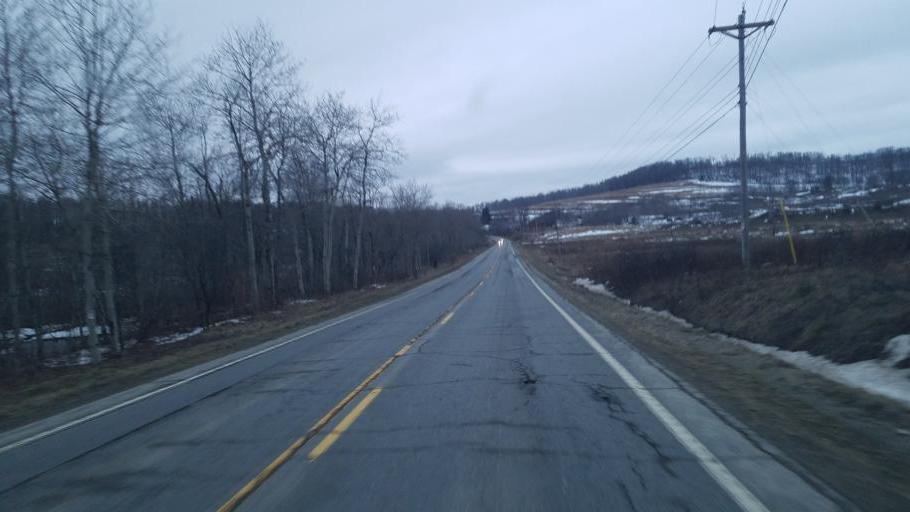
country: US
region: Pennsylvania
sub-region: Potter County
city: Coudersport
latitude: 41.8562
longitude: -77.8720
